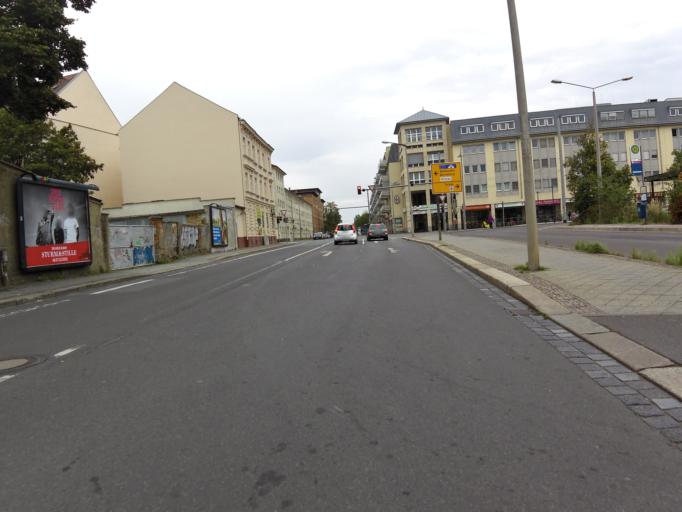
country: DE
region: Saxony
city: Leipzig
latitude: 51.3310
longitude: 12.3191
